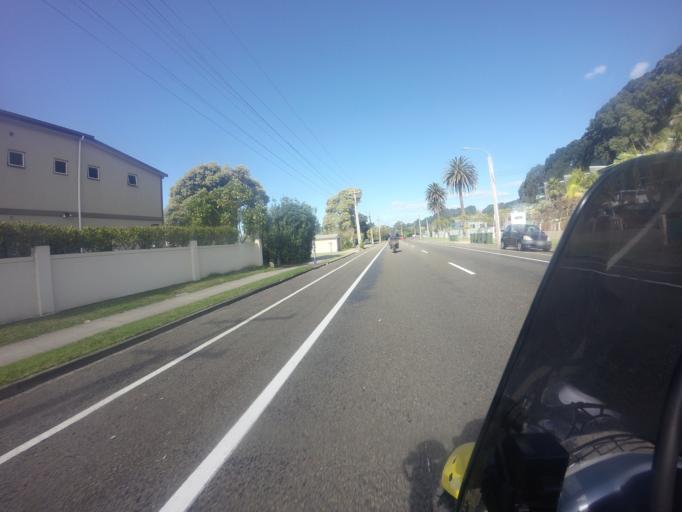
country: NZ
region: Bay of Plenty
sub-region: Whakatane District
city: Whakatane
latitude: -37.9706
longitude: 177.0547
